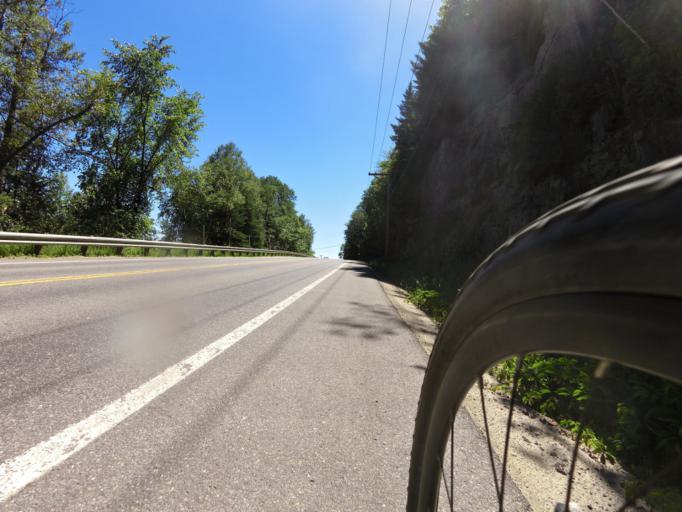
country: CA
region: Quebec
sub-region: Laurentides
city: Mont-Tremblant
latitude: 46.1080
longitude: -74.6090
